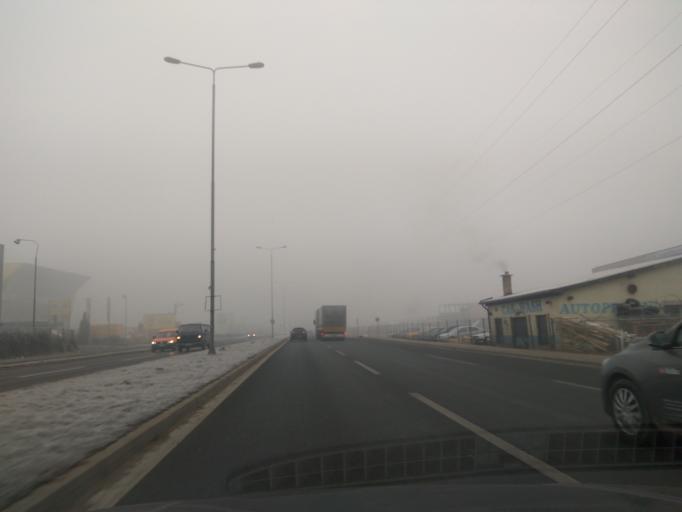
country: BA
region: Federation of Bosnia and Herzegovina
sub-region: Kanton Sarajevo
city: Sarajevo
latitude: 43.8495
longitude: 18.3268
